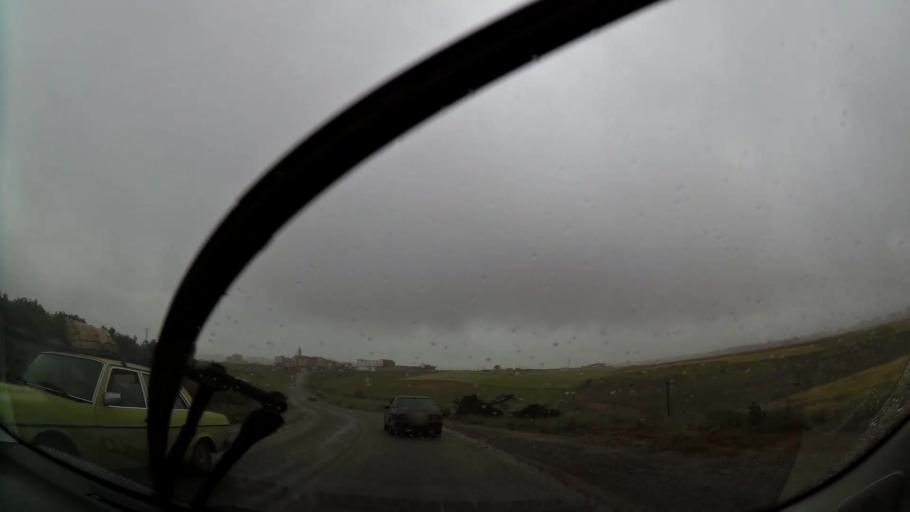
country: MA
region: Oriental
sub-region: Nador
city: Boudinar
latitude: 35.1289
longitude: -3.6293
